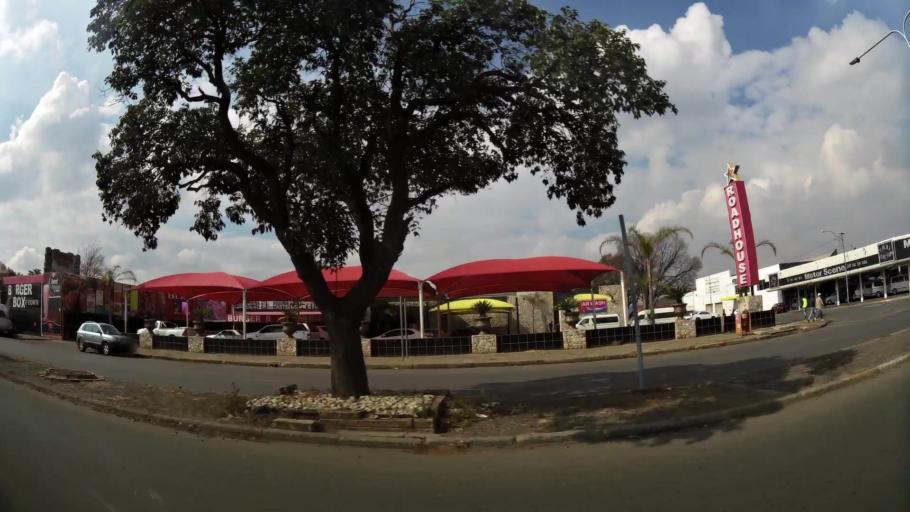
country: ZA
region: Gauteng
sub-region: Sedibeng District Municipality
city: Vereeniging
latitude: -26.6831
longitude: 27.9297
